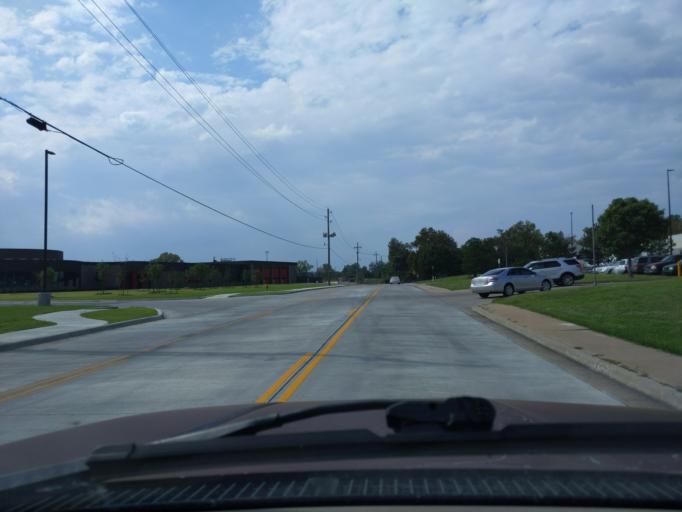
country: US
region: Oklahoma
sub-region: Tulsa County
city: Sand Springs
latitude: 36.1336
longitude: -96.1193
